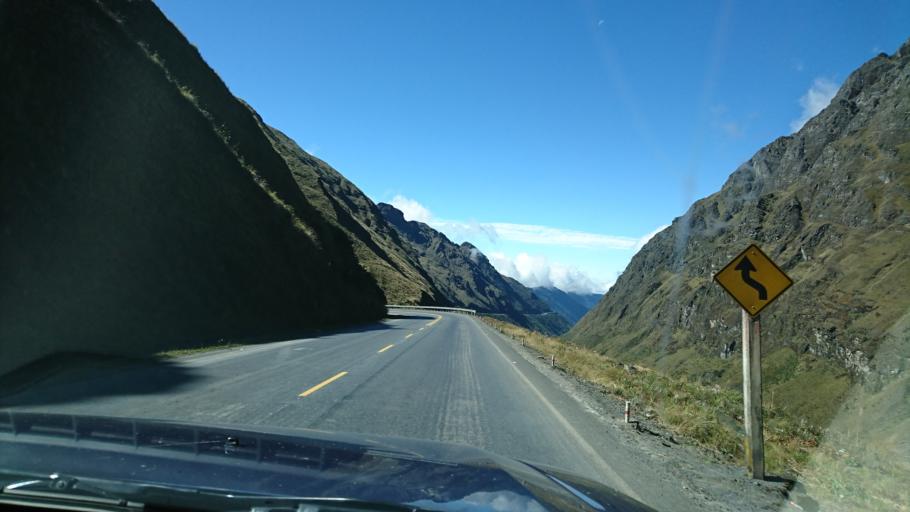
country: BO
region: La Paz
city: Coroico
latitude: -16.3268
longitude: -67.9419
